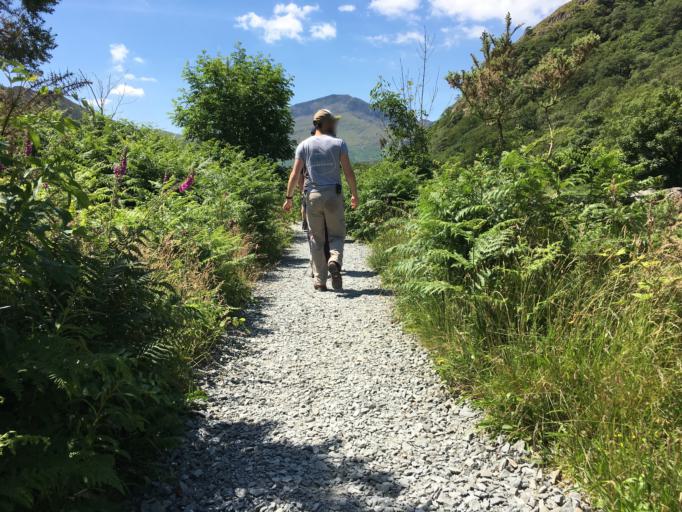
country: GB
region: Wales
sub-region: Gwynedd
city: Penrhyndeudraeth
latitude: 53.0220
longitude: -4.0744
